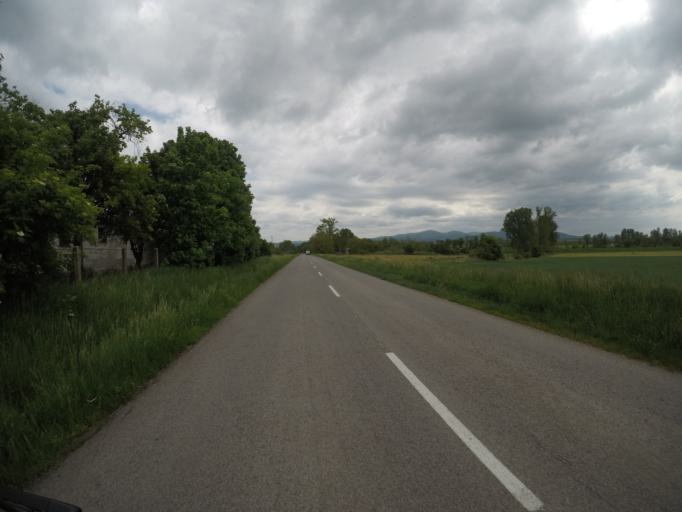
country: SK
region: Nitriansky
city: Sahy
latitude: 48.0675
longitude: 18.8462
